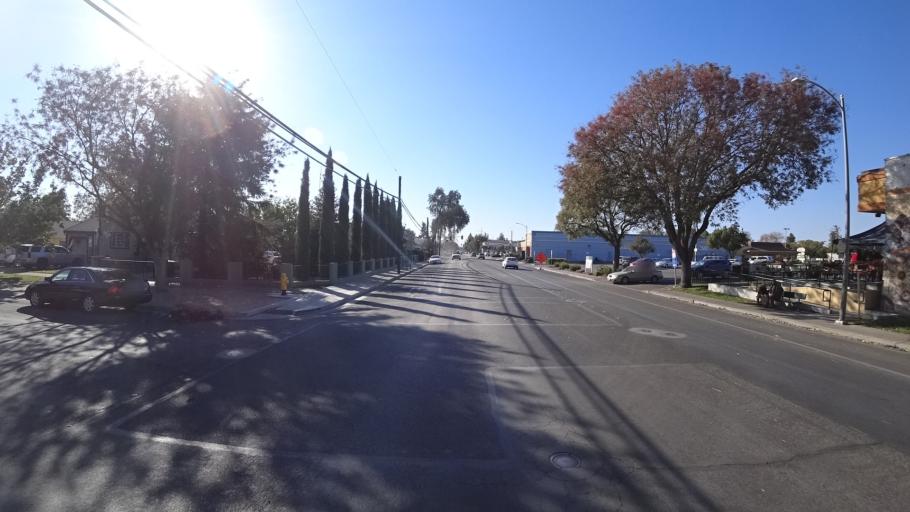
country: US
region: California
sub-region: Yolo County
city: Woodland
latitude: 38.6800
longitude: -121.7840
